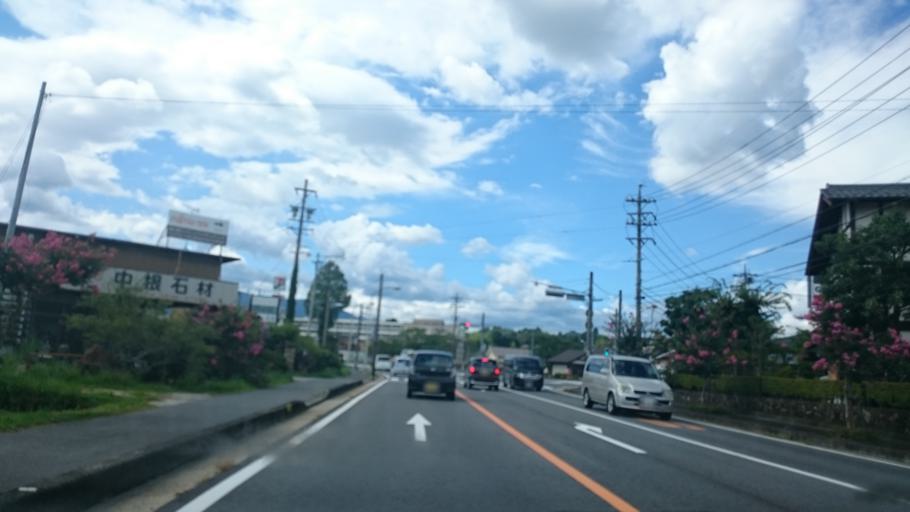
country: JP
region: Gifu
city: Nakatsugawa
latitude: 35.5216
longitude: 137.4747
